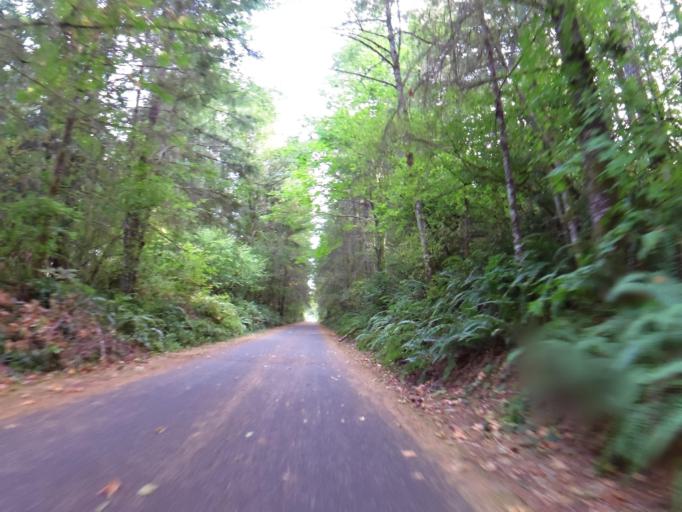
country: US
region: Washington
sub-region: Thurston County
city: Lacey
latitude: 46.9703
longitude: -122.8129
